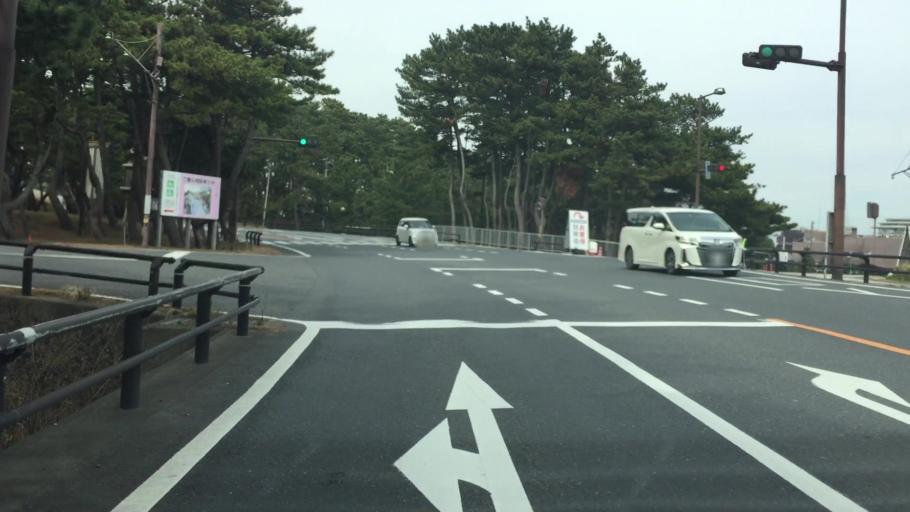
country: JP
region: Ibaraki
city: Oarai
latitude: 36.3307
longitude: 140.5930
